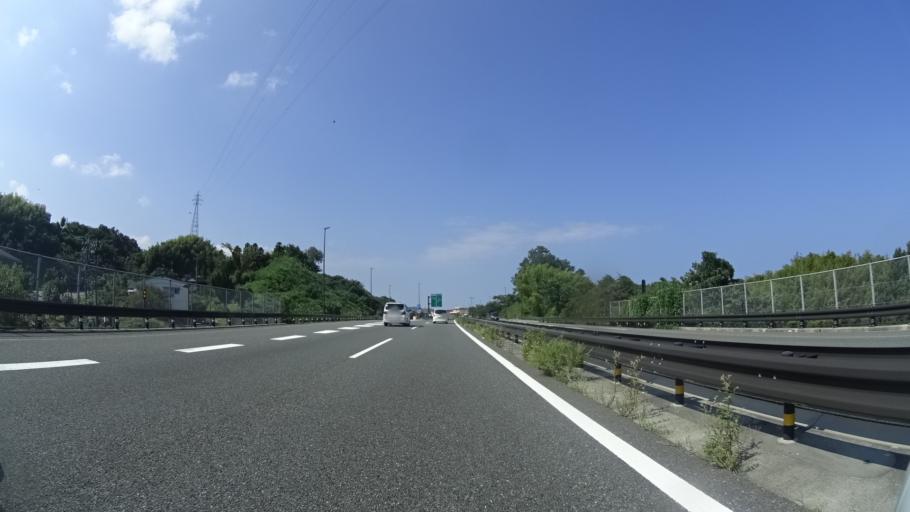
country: JP
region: Shimane
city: Hamada
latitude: 34.8914
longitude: 132.0771
